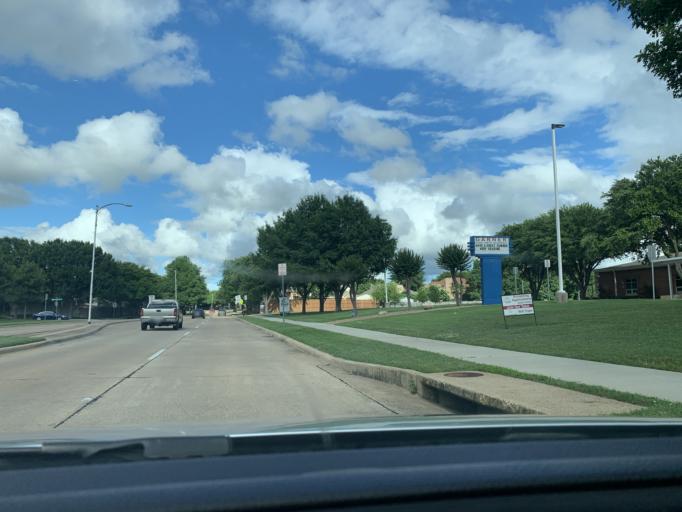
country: US
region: Texas
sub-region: Dallas County
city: Grand Prairie
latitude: 32.6583
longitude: -97.0109
